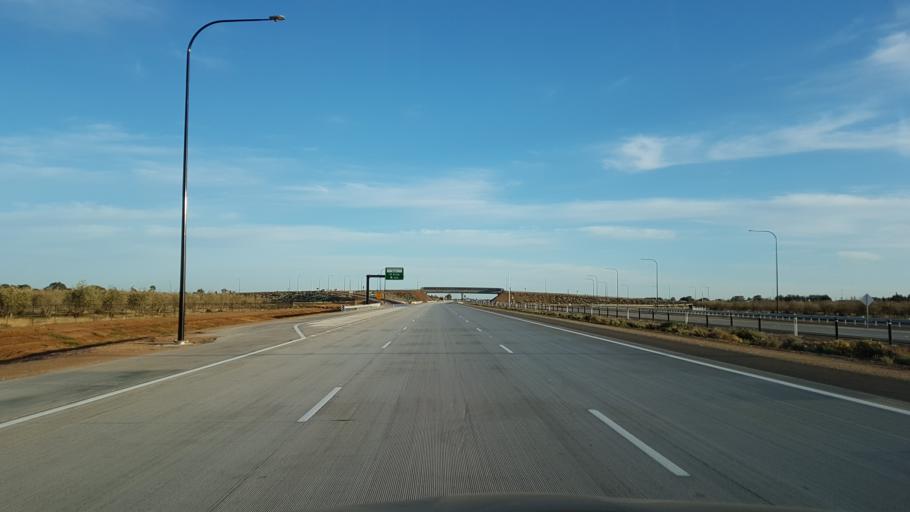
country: AU
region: South Australia
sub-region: Salisbury
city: Salisbury
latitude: -34.7377
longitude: 138.5782
